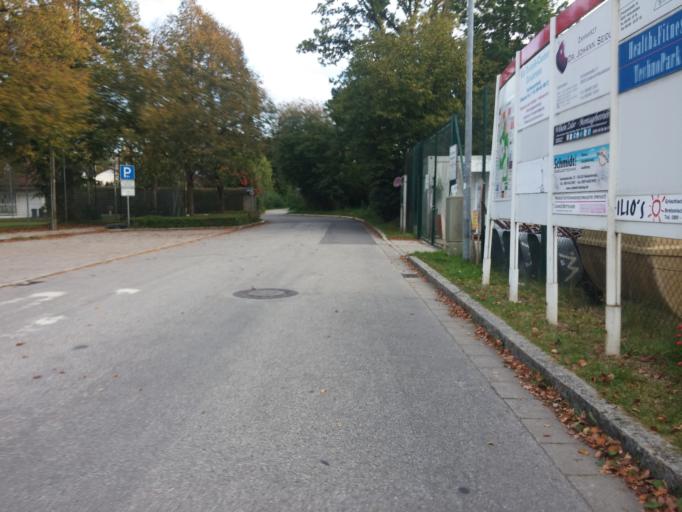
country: DE
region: Bavaria
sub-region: Upper Bavaria
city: Vaterstetten
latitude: 48.0925
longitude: 11.7587
